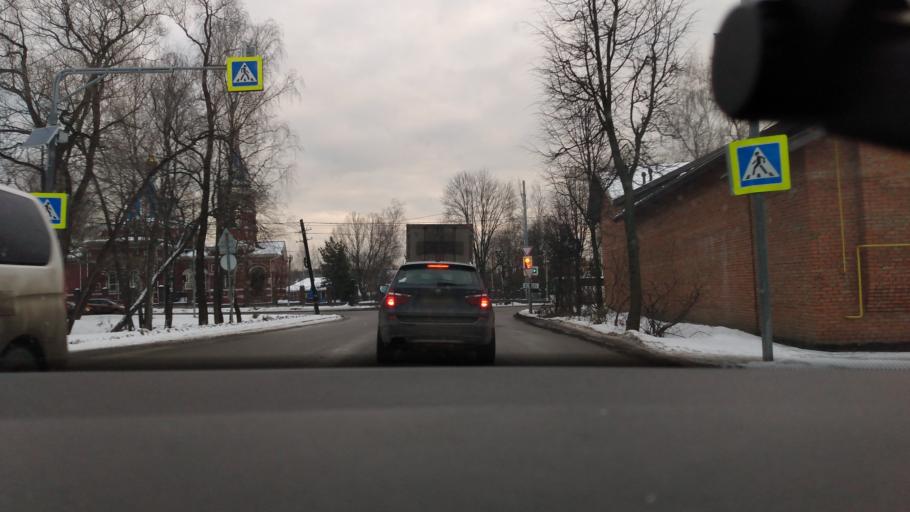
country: RU
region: Moskovskaya
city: Bykovo
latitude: 55.6569
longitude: 38.1011
